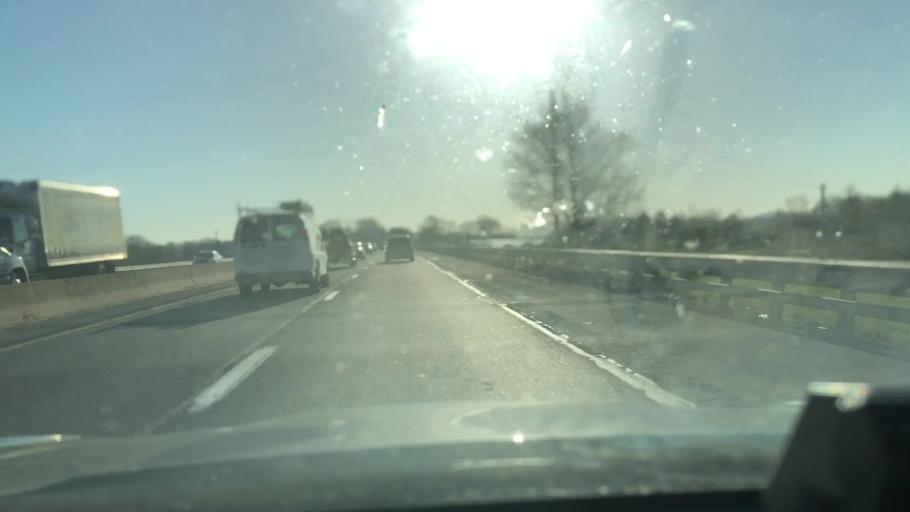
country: US
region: Pennsylvania
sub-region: Northampton County
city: Middletown
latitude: 40.6823
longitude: -75.3154
